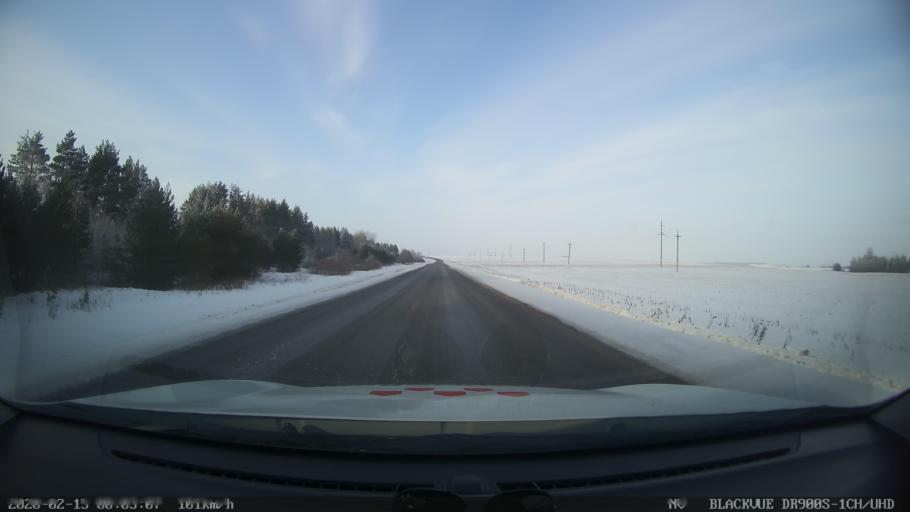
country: RU
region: Tatarstan
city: Kuybyshevskiy Zaton
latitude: 55.3675
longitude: 48.9998
